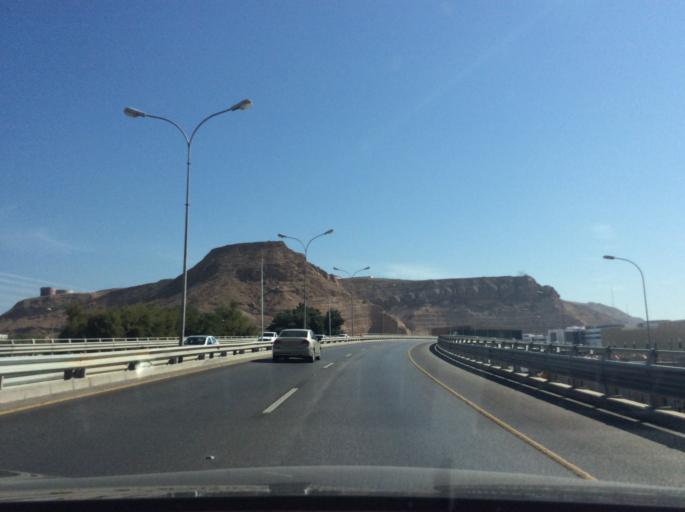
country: OM
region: Muhafazat Masqat
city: Muscat
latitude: 23.6070
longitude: 58.5089
